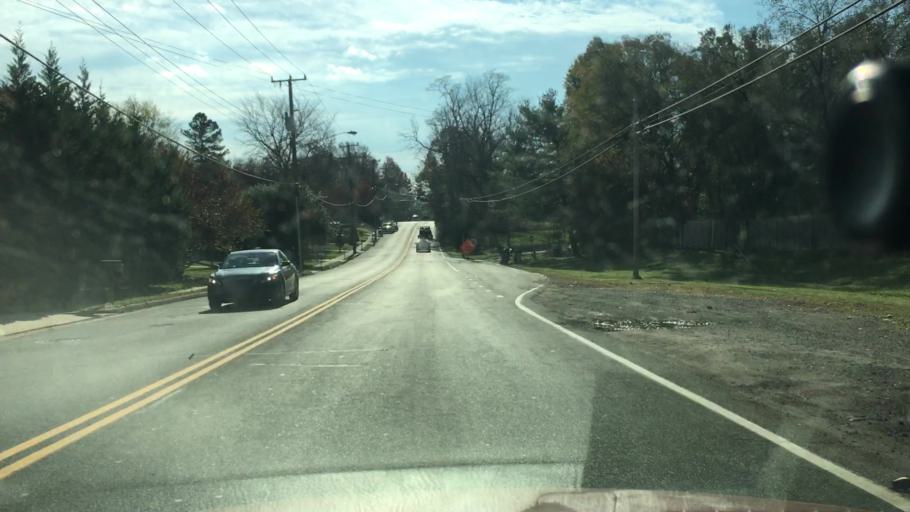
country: US
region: Virginia
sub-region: Fairfax County
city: Pimmit Hills
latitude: 38.9114
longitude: -77.1845
